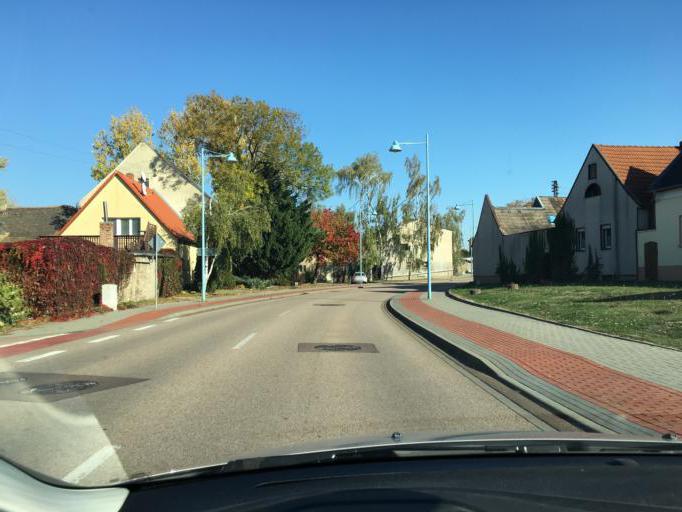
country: DE
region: Saxony-Anhalt
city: Bernburg
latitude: 51.7995
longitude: 11.7770
